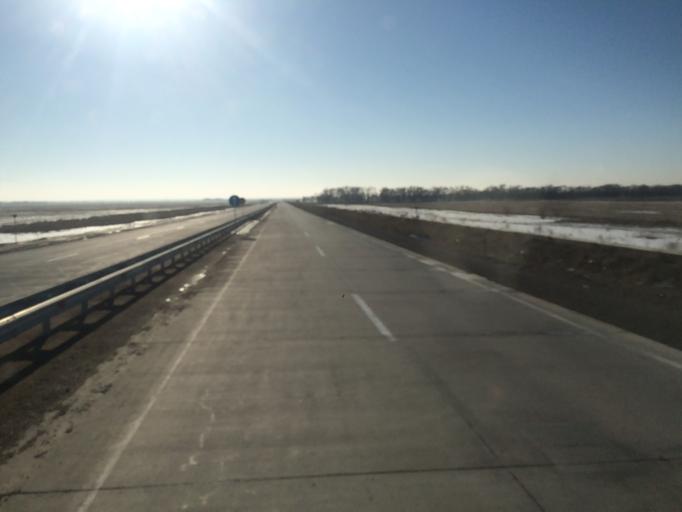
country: KG
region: Chuy
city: Sokuluk
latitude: 43.3003
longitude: 74.2511
